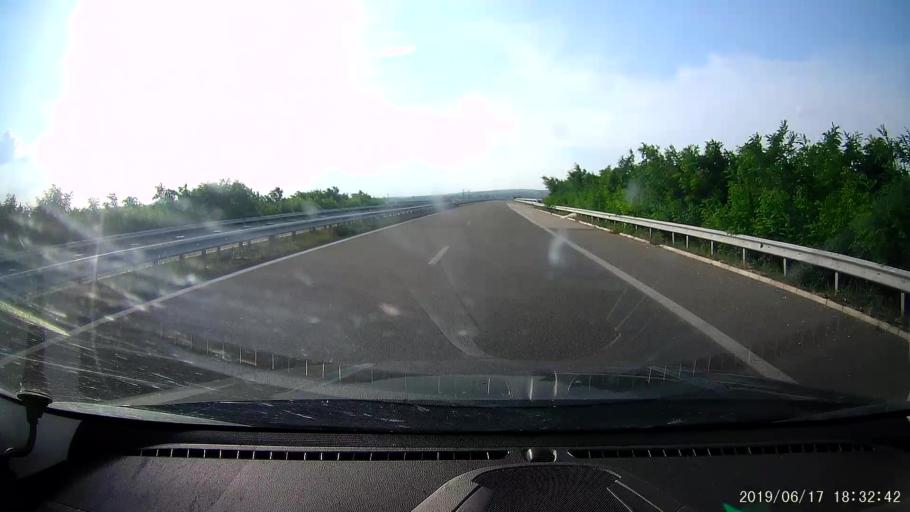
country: BG
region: Khaskovo
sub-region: Obshtina Dimitrovgrad
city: Dimitrovgrad
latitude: 42.0644
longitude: 25.4729
